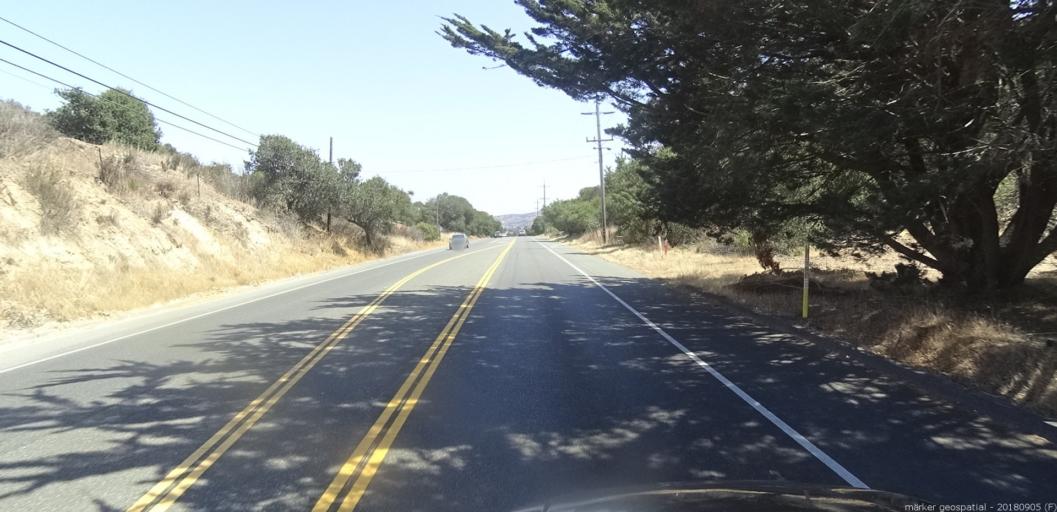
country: US
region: California
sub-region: Monterey County
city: Carmel Valley Village
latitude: 36.5706
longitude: -121.7487
